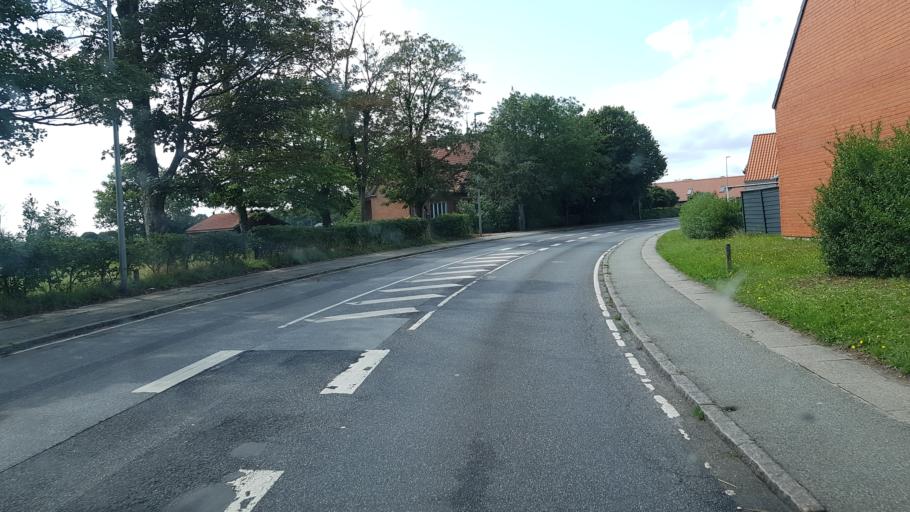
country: DK
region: South Denmark
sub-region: Vejen Kommune
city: Vejen
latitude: 55.5704
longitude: 9.1457
